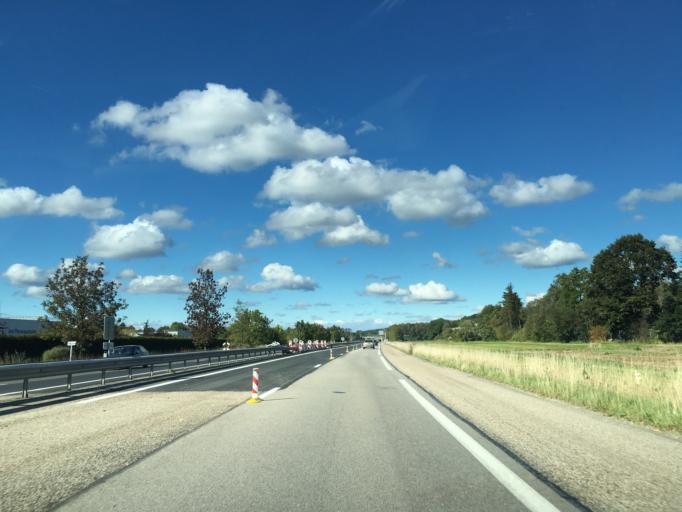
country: FR
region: Lorraine
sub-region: Departement des Vosges
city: Saint-Die-des-Vosges
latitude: 48.3035
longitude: 6.9249
